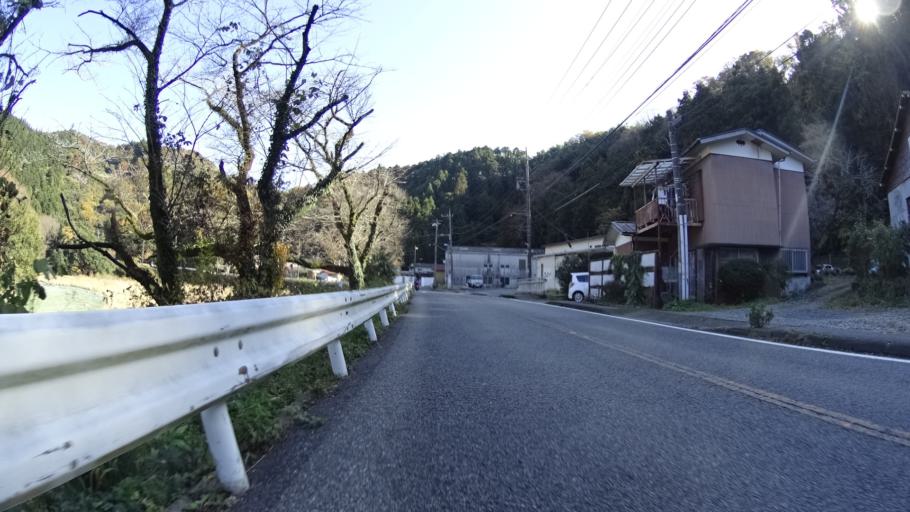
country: JP
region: Kanagawa
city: Zama
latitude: 35.5355
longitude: 139.2799
